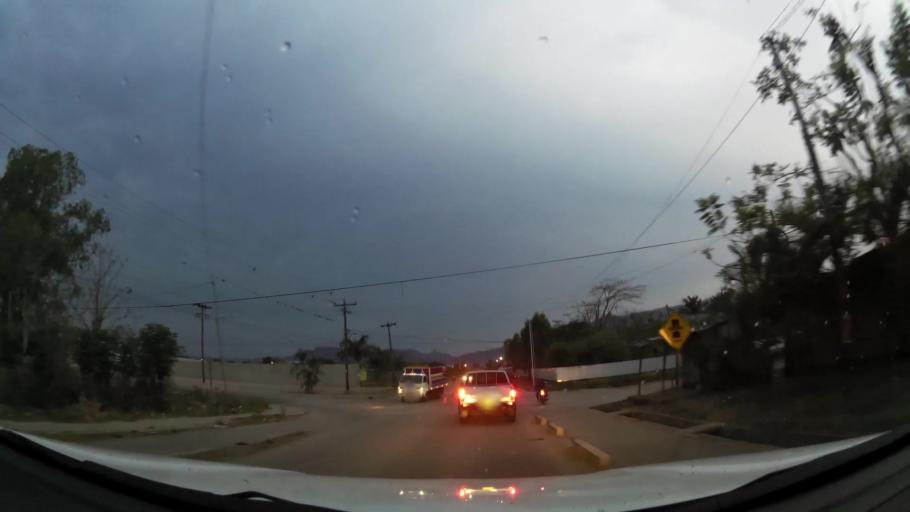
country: NI
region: Esteli
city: Esteli
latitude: 13.1069
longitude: -86.3592
